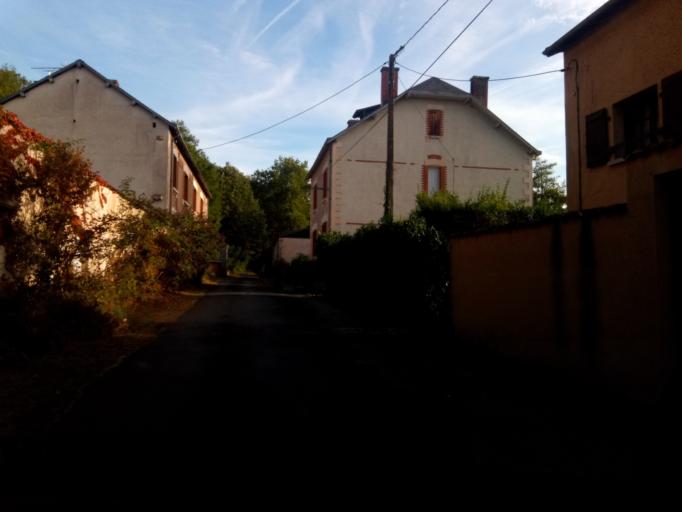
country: FR
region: Poitou-Charentes
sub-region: Departement de la Vienne
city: Saulge
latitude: 46.4041
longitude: 0.8764
